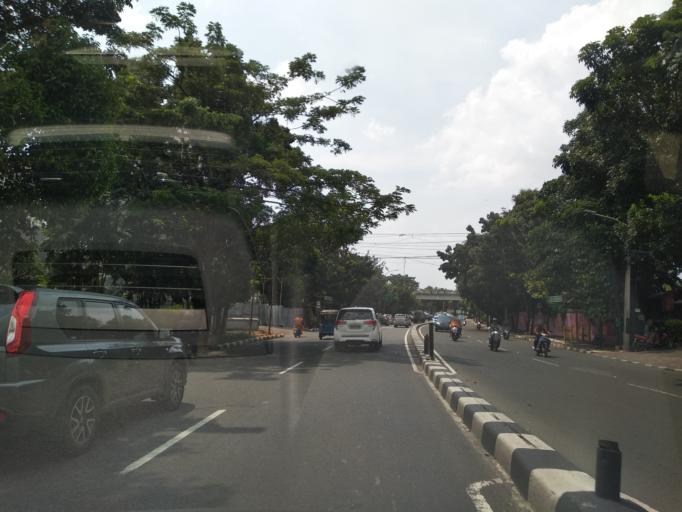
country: ID
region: Jakarta Raya
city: Jakarta
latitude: -6.2252
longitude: 106.8474
